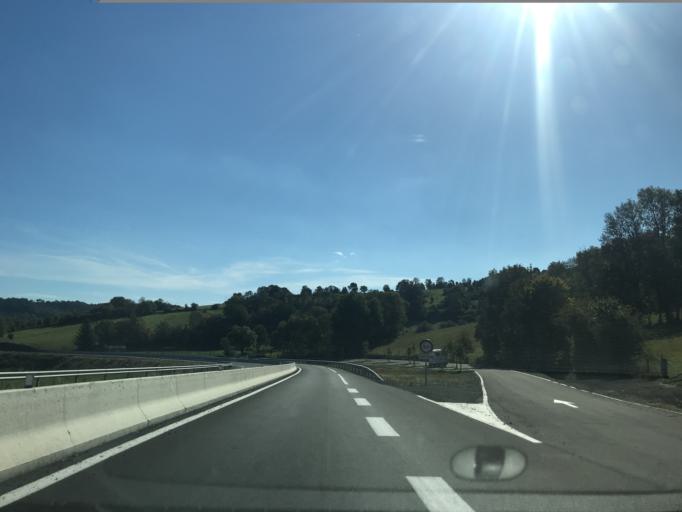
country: FR
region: Auvergne
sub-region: Departement du Puy-de-Dome
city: Gelles
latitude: 45.7327
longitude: 2.8210
